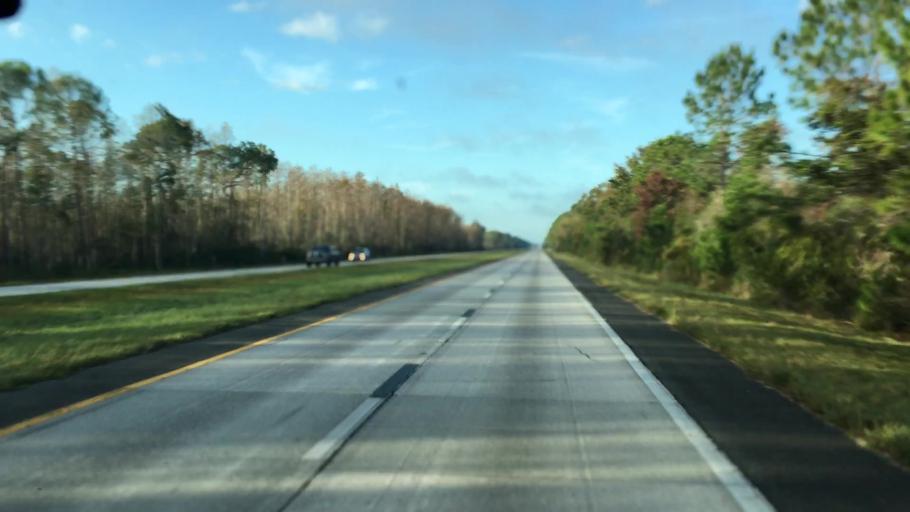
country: US
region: Florida
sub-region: Volusia County
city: North DeLand
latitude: 29.0953
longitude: -81.2239
